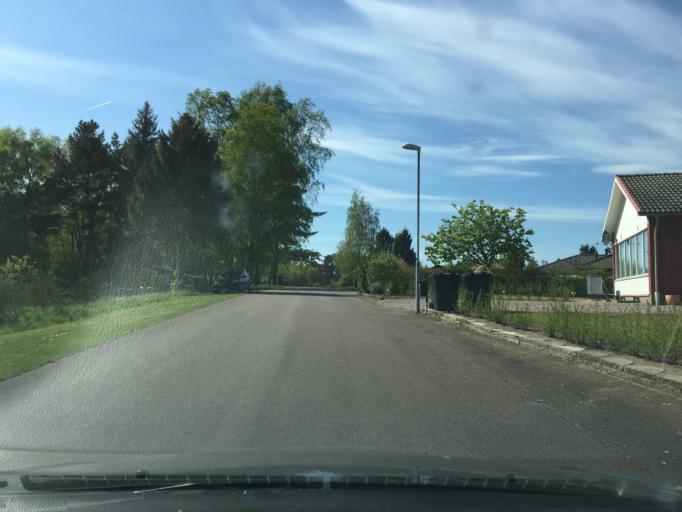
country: SE
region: Skane
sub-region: Sjobo Kommun
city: Blentarp
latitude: 55.5809
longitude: 13.6040
